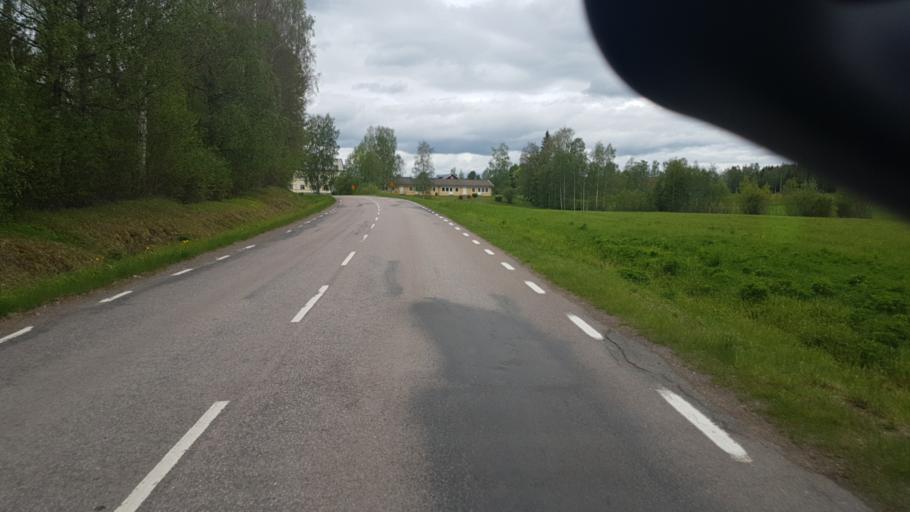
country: SE
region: Vaermland
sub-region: Arvika Kommun
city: Arvika
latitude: 59.8134
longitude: 12.5822
